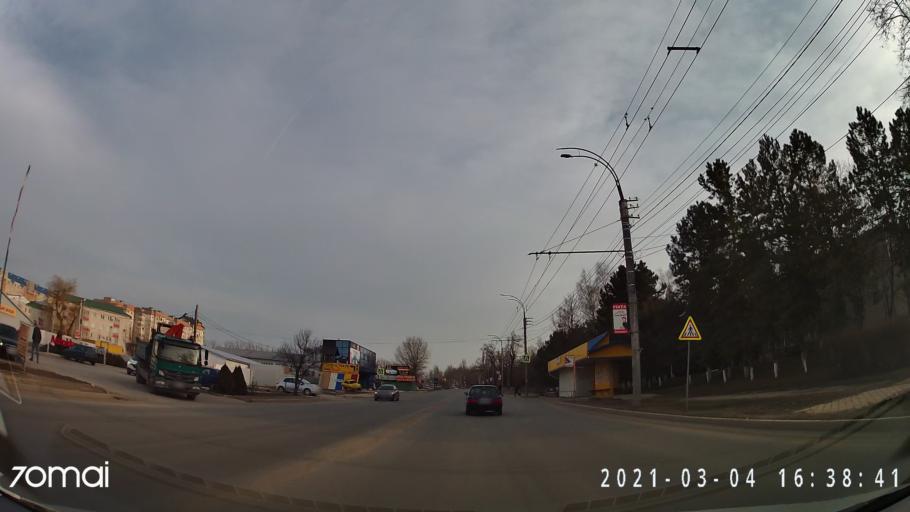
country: MD
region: Balti
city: Balti
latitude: 47.7794
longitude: 27.8923
